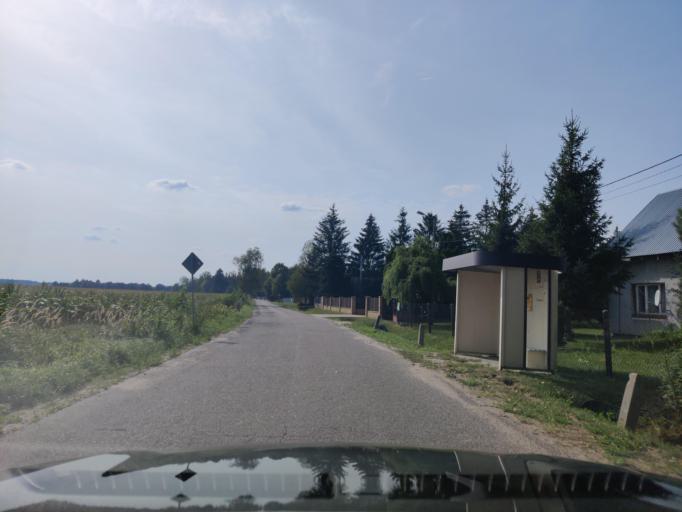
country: PL
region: Masovian Voivodeship
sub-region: Powiat pultuski
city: Obryte
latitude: 52.7718
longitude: 21.2617
